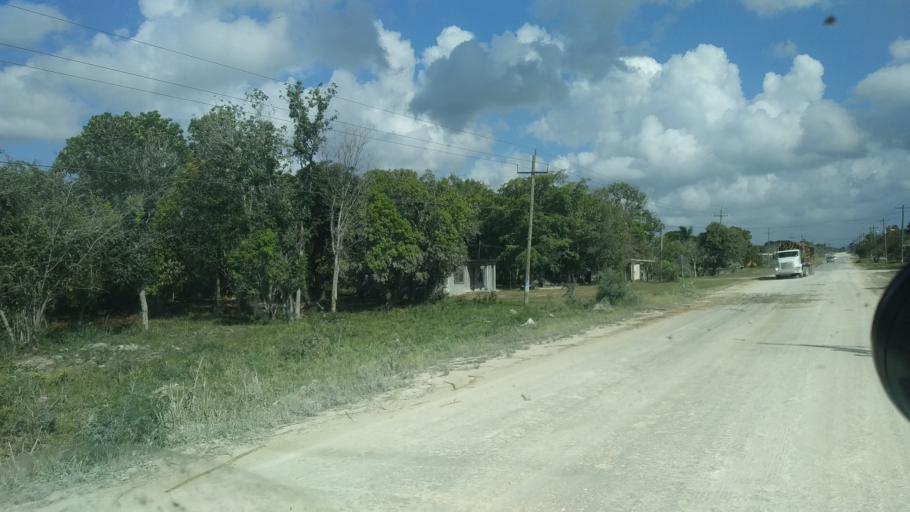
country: BZ
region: Corozal
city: Corozal
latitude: 18.3354
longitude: -88.4956
